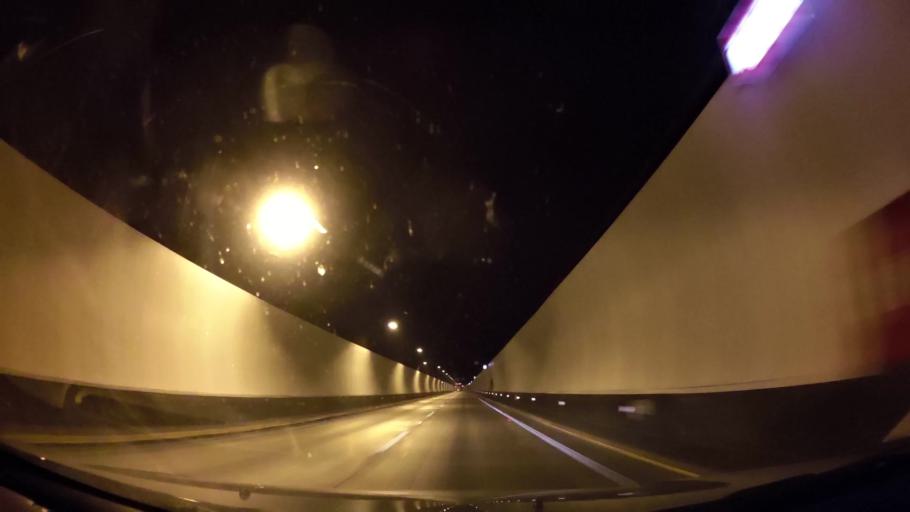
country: CL
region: Santiago Metropolitan
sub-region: Provincia de Santiago
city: Santiago
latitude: -33.4135
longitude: -70.6136
